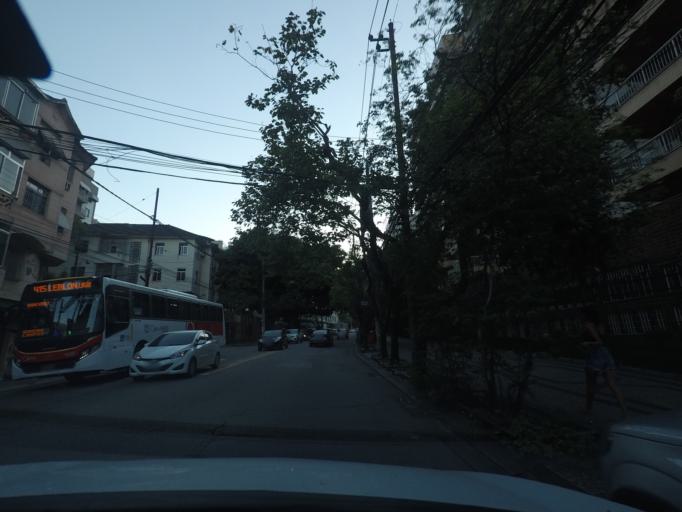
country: BR
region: Rio de Janeiro
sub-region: Rio De Janeiro
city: Rio de Janeiro
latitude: -22.9402
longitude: -43.2494
